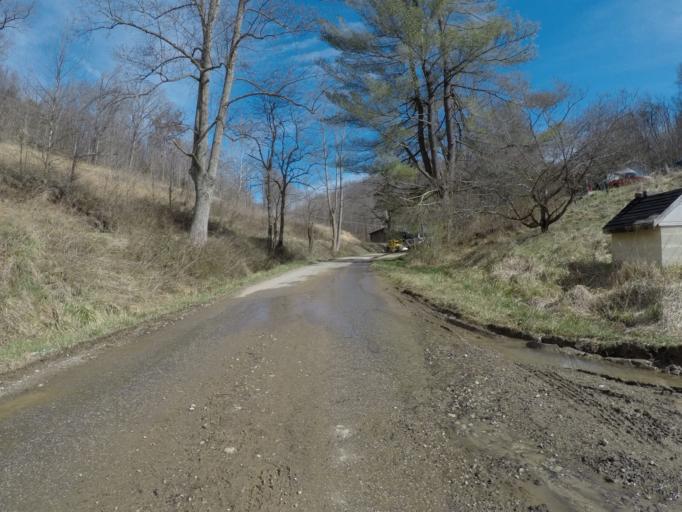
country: US
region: West Virginia
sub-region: Wayne County
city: Ceredo
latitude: 38.3480
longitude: -82.5547
